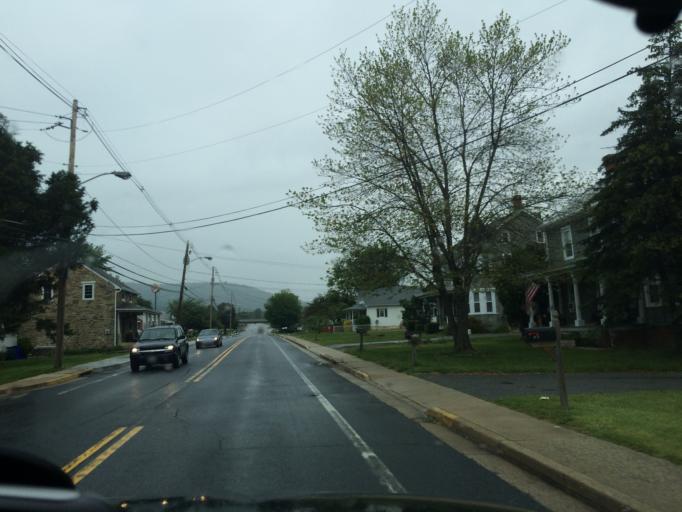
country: US
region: Maryland
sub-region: Frederick County
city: Thurmont
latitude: 39.6308
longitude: -77.4107
